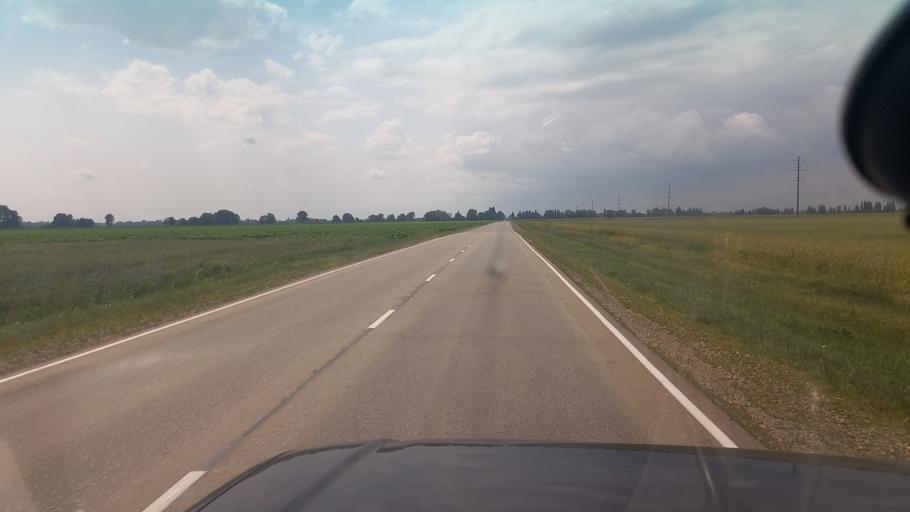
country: RU
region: Adygeya
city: Koshekhabl'
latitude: 44.9062
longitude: 40.4630
